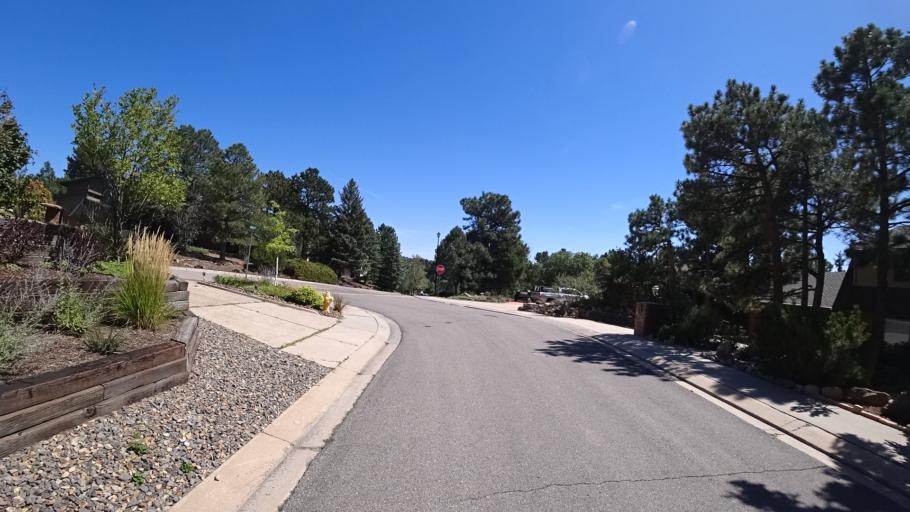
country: US
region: Colorado
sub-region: El Paso County
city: Colorado Springs
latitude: 38.9187
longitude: -104.7966
